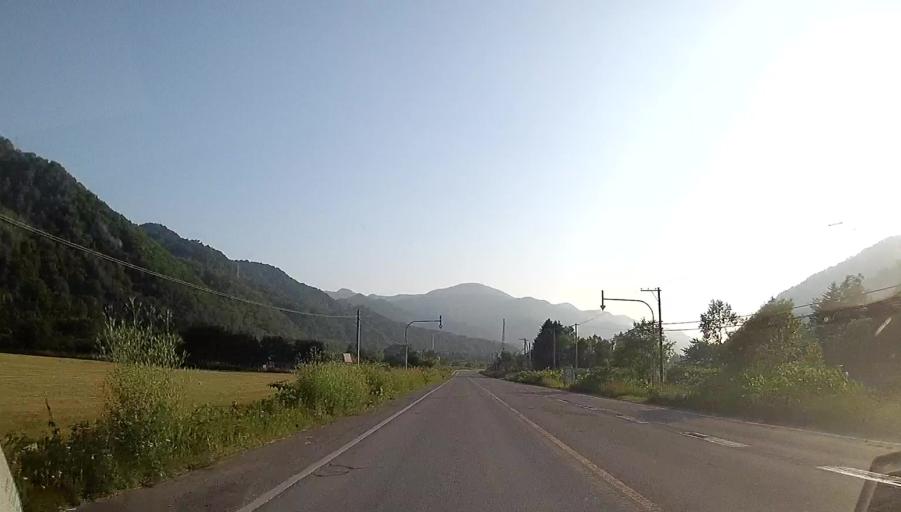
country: JP
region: Hokkaido
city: Shimo-furano
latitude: 42.8966
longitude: 142.5574
